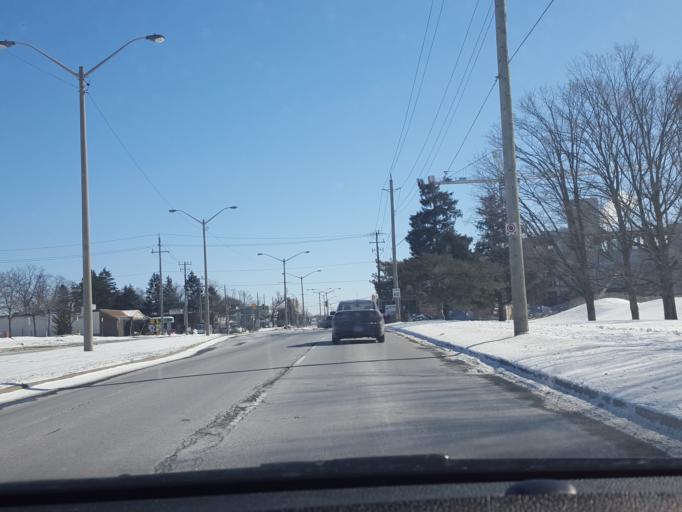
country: CA
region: Ontario
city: Cambridge
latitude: 43.3806
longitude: -80.3310
